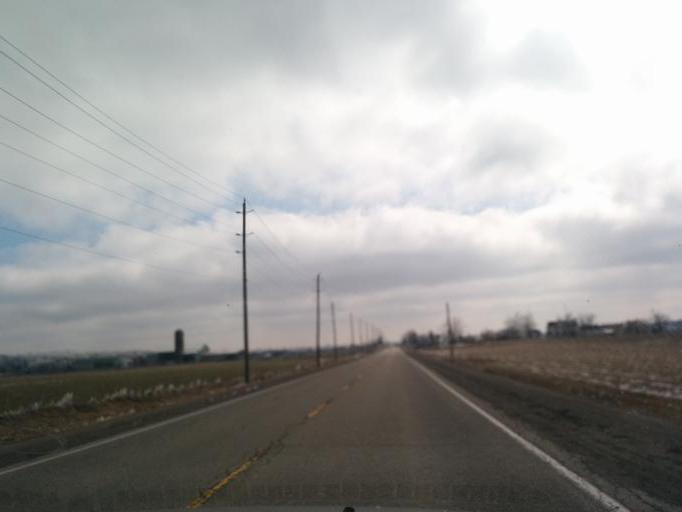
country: CA
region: Ontario
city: Waterloo
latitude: 43.6482
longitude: -80.5471
